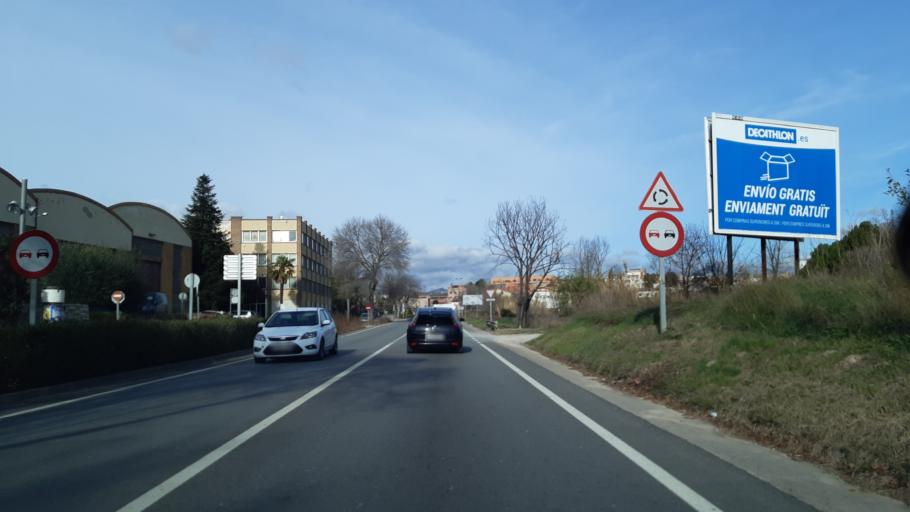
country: ES
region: Catalonia
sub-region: Provincia de Barcelona
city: Vilanova del Cami
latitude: 41.5763
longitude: 1.6407
